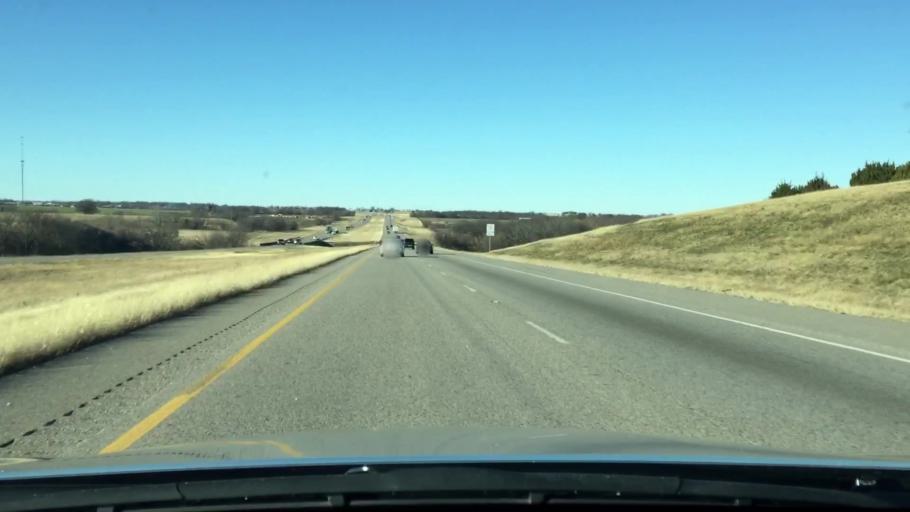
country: US
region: Texas
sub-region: Johnson County
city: Grandview
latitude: 32.2399
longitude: -97.1560
